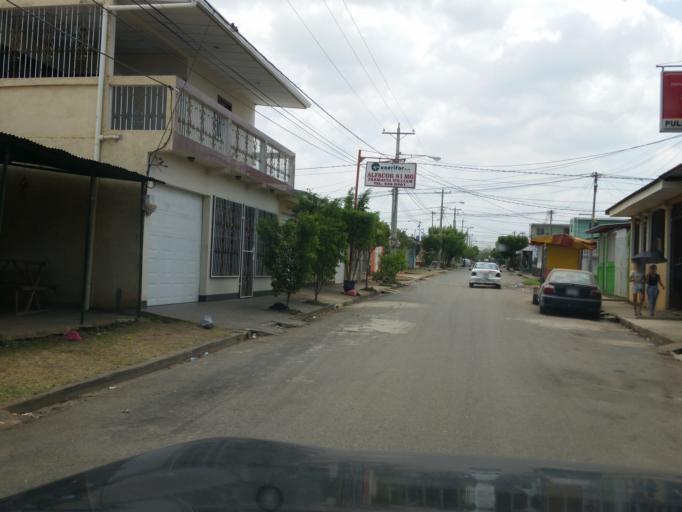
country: NI
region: Managua
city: Managua
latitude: 12.1310
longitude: -86.1888
